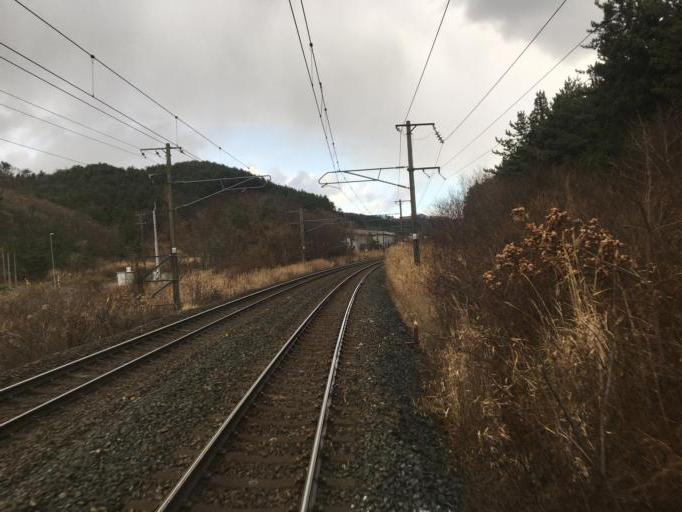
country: JP
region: Aomori
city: Aomori Shi
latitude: 40.9163
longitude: 140.8774
